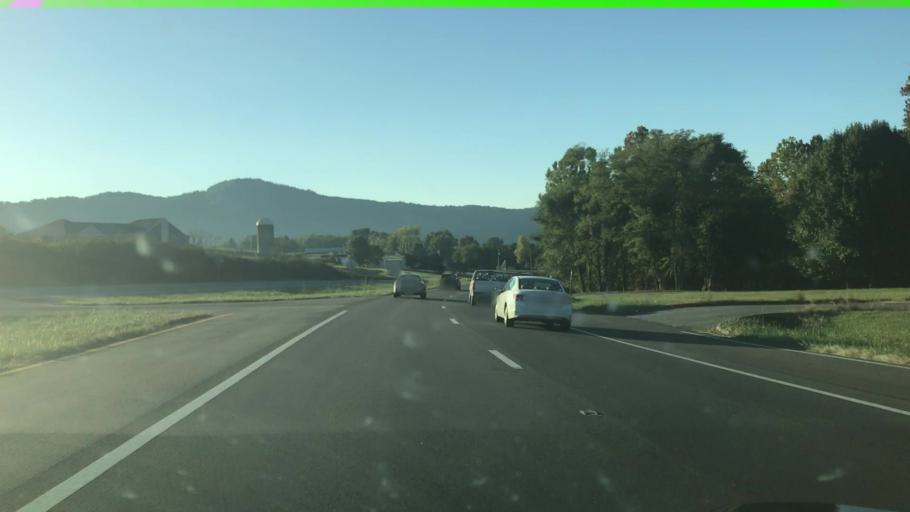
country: US
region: Virginia
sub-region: Botetourt County
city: Laymantown
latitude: 37.3408
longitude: -79.8764
